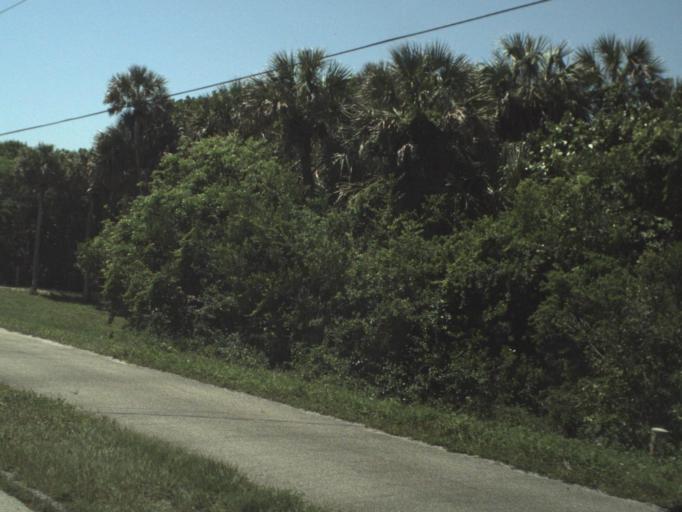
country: US
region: Florida
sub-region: Brevard County
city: Micco
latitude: 27.8893
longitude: -80.4640
